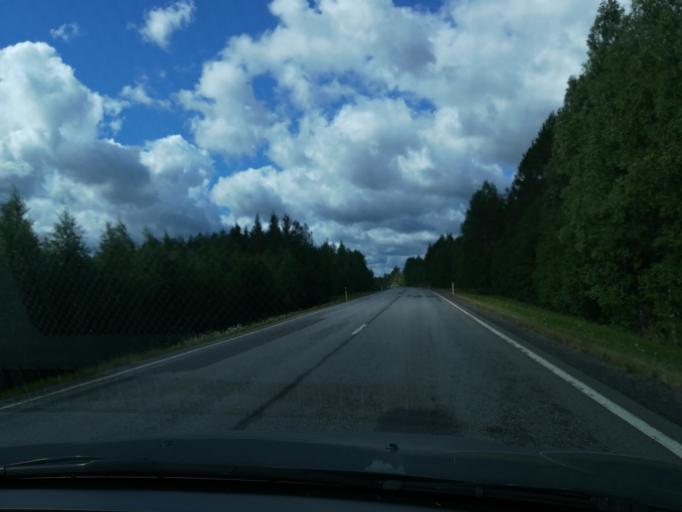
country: FI
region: Southern Savonia
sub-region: Mikkeli
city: Ristiina
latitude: 61.4308
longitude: 27.2348
